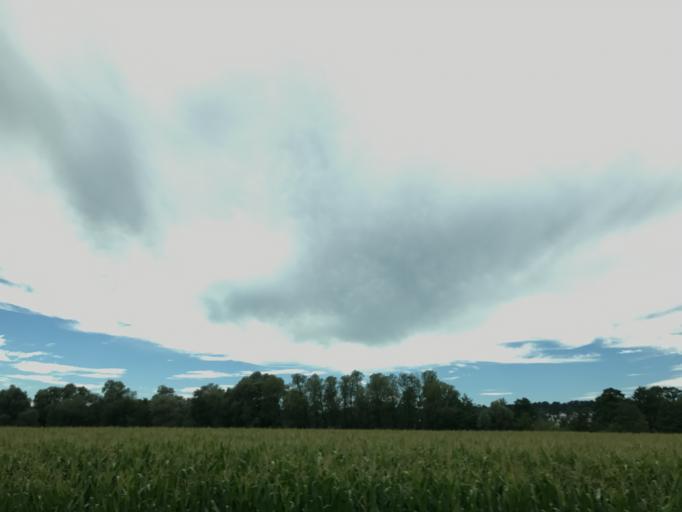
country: DE
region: Baden-Wuerttemberg
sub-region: Tuebingen Region
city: Berg
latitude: 47.8364
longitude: 9.6121
